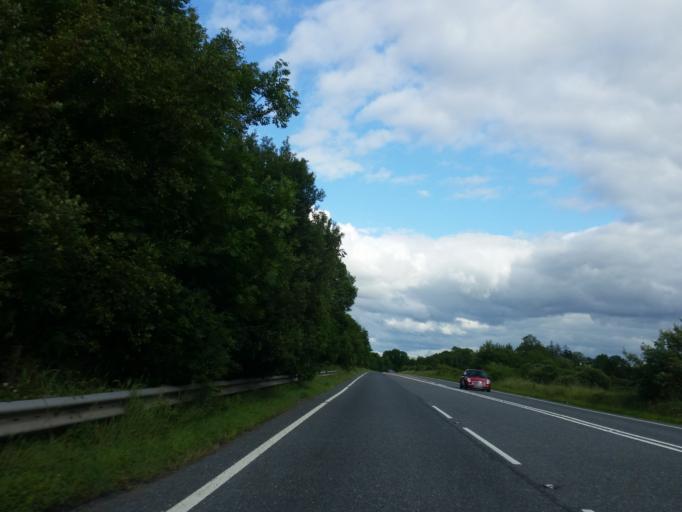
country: GB
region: Northern Ireland
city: Lisnaskea
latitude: 54.3133
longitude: -7.5081
